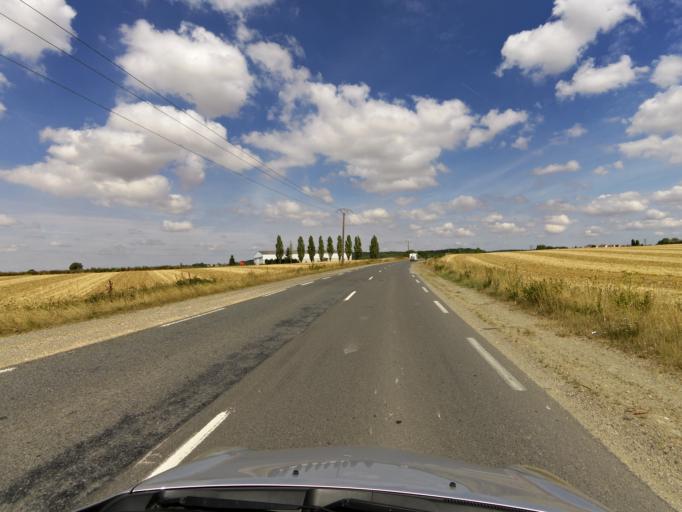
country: FR
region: Ile-de-France
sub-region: Departement de Seine-et-Marne
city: Chauconin-Neufmontiers
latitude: 48.9698
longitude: 2.8570
